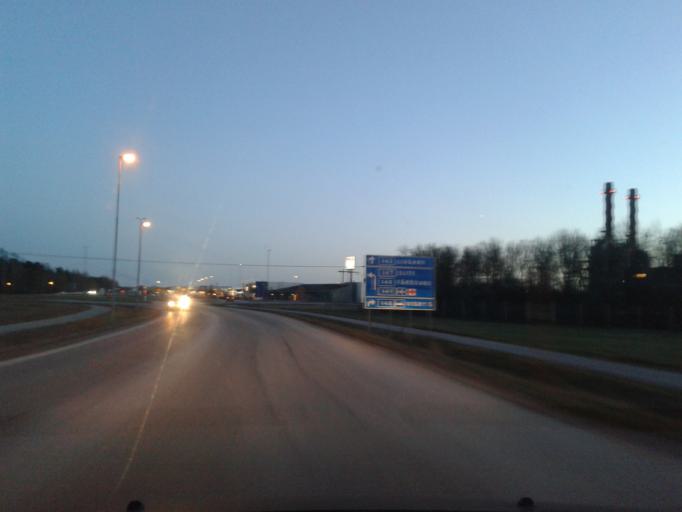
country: SE
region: Gotland
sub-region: Gotland
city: Visby
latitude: 57.6262
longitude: 18.3190
